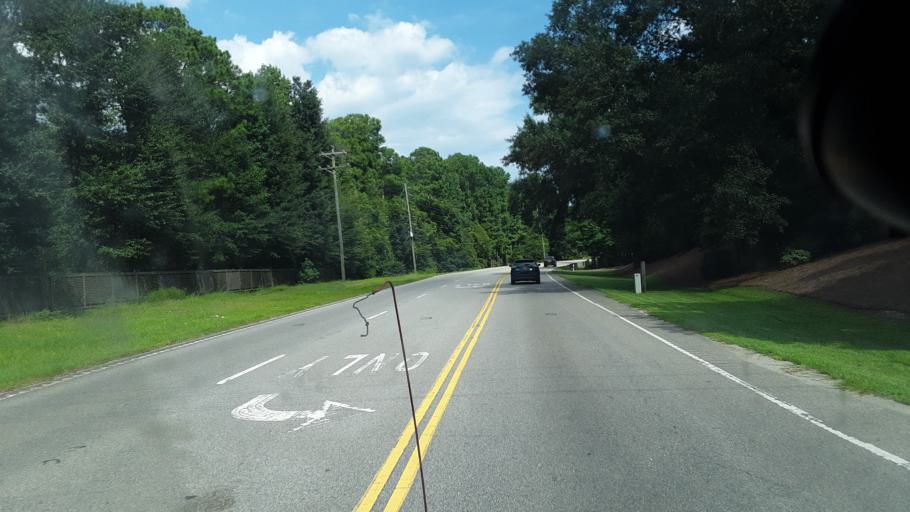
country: US
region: South Carolina
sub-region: Horry County
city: Red Hill
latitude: 33.8222
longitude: -78.9264
